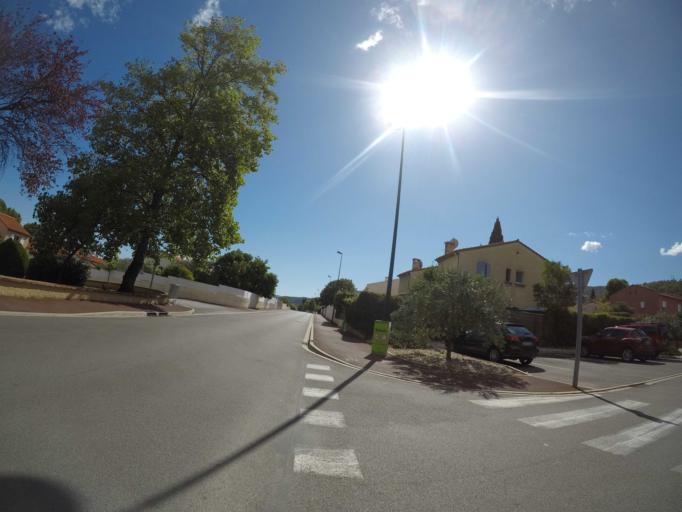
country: FR
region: Languedoc-Roussillon
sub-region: Departement des Pyrenees-Orientales
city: Ceret
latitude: 42.4930
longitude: 2.7359
